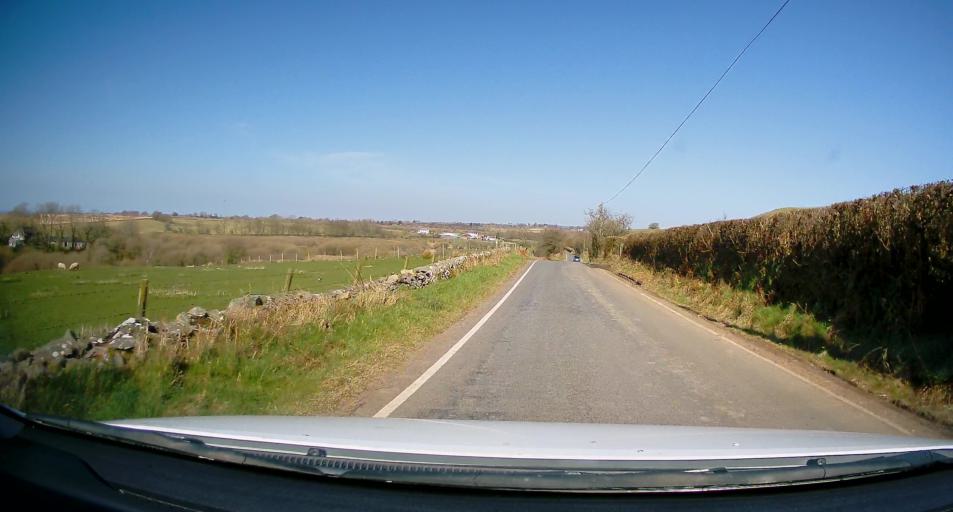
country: GB
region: Wales
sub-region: County of Ceredigion
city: Lledrod
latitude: 52.2773
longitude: -4.0641
